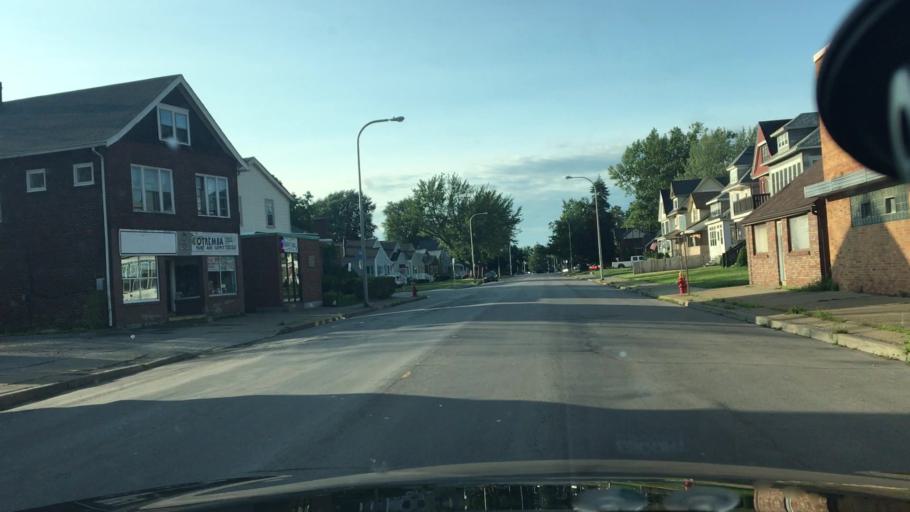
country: US
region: New York
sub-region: Erie County
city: West Seneca
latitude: 42.8422
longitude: -78.8088
